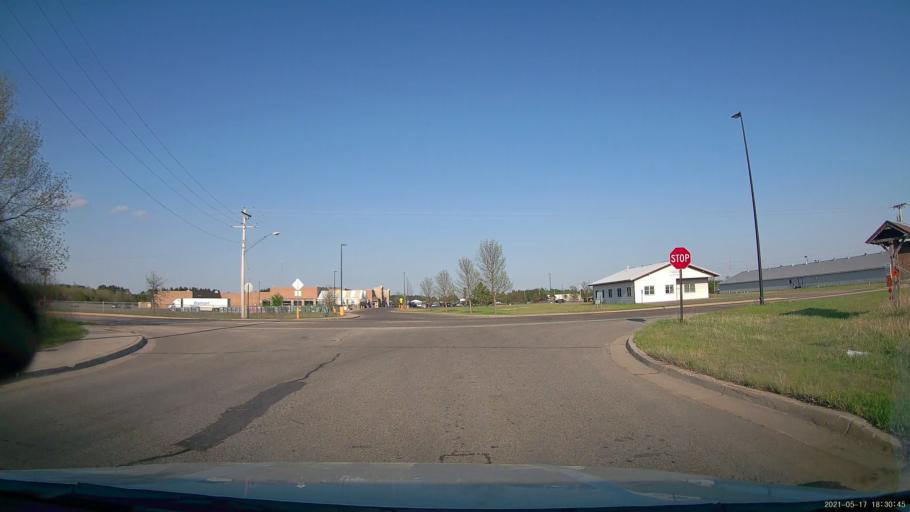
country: US
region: Minnesota
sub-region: Hubbard County
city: Park Rapids
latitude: 46.9247
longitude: -95.0373
